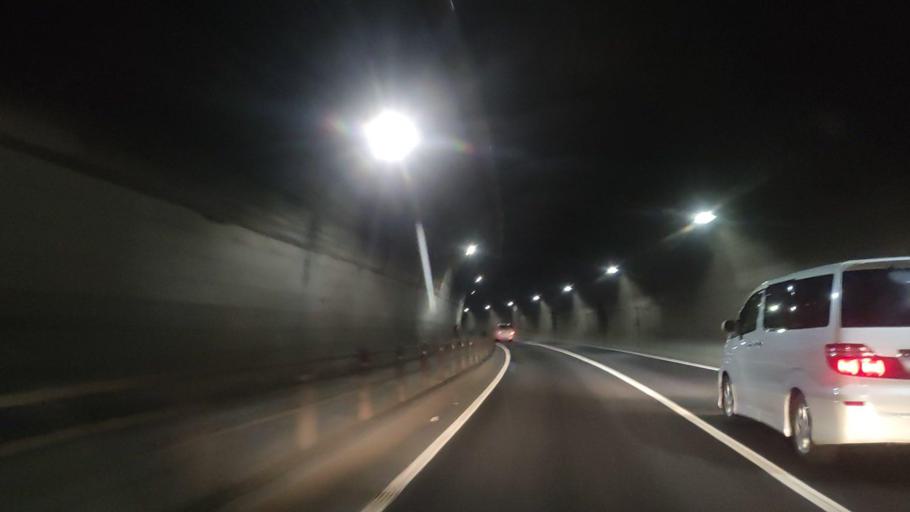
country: JP
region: Hokkaido
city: Otaru
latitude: 43.1799
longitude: 141.0345
